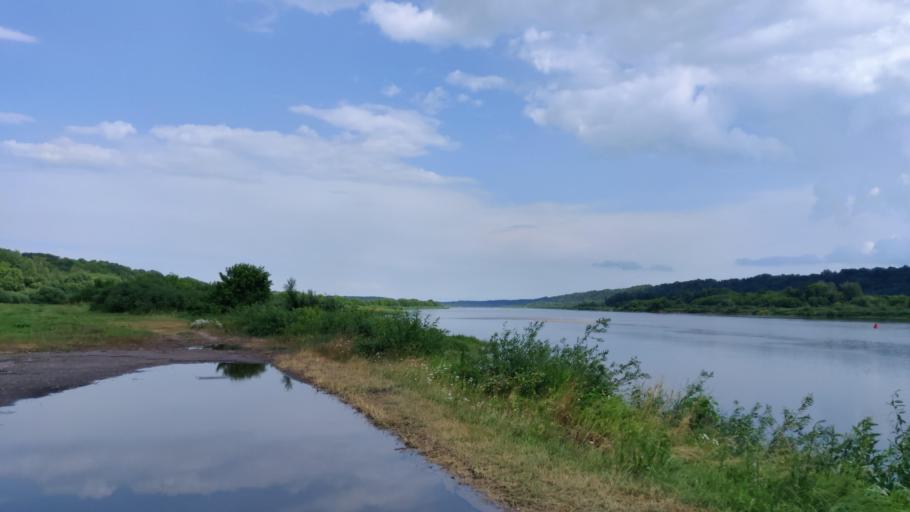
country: LT
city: Gelgaudiskis
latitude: 55.1057
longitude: 23.0610
